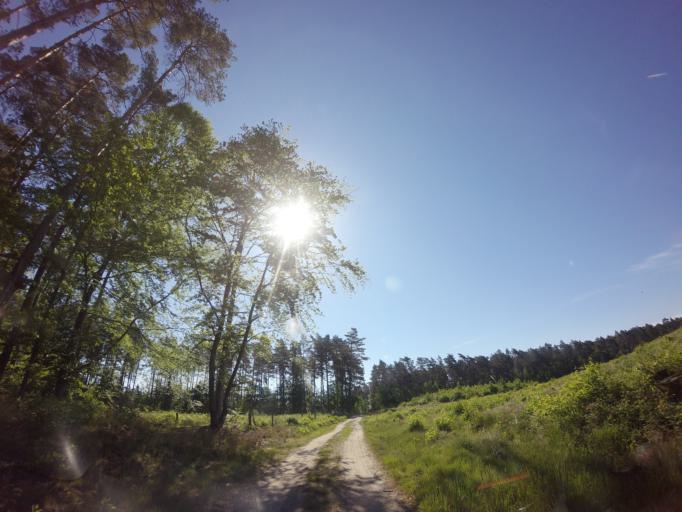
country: PL
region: West Pomeranian Voivodeship
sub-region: Powiat choszczenski
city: Drawno
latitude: 53.2355
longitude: 15.6827
